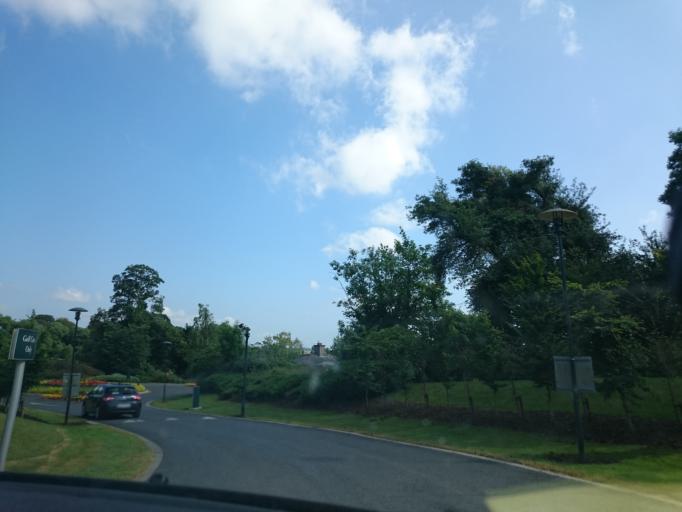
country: IE
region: Leinster
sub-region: Kilkenny
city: Thomastown
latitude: 52.5206
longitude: -7.1913
